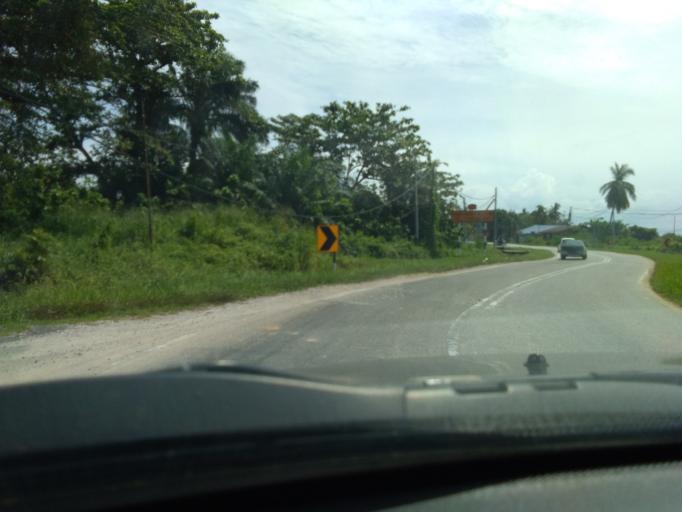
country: MY
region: Perak
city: Bagan Serai
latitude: 5.0143
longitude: 100.5388
